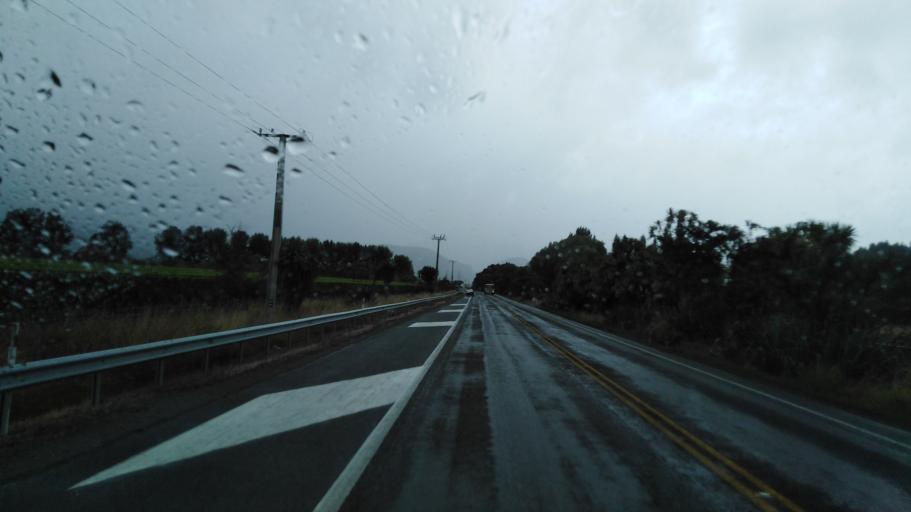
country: NZ
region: Marlborough
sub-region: Marlborough District
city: Blenheim
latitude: -41.4499
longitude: 173.9640
